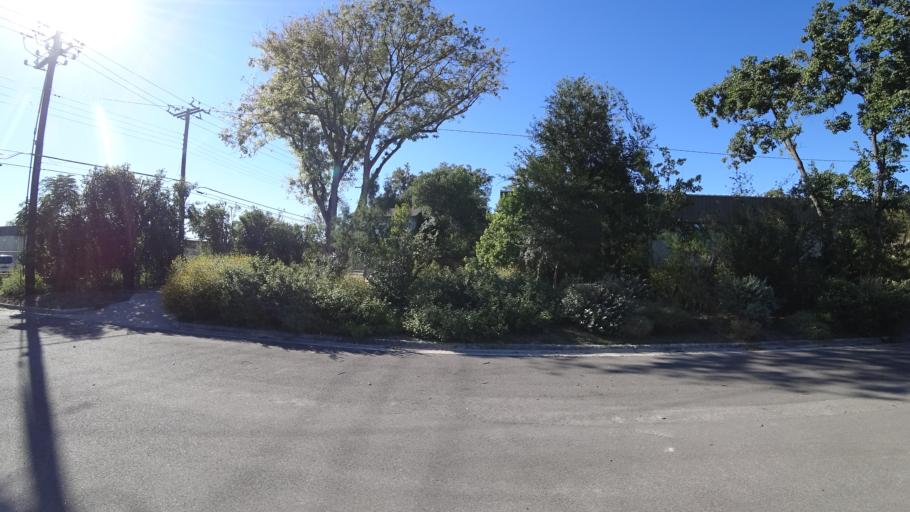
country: US
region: Texas
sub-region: Travis County
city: West Lake Hills
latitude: 30.3270
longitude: -97.7604
